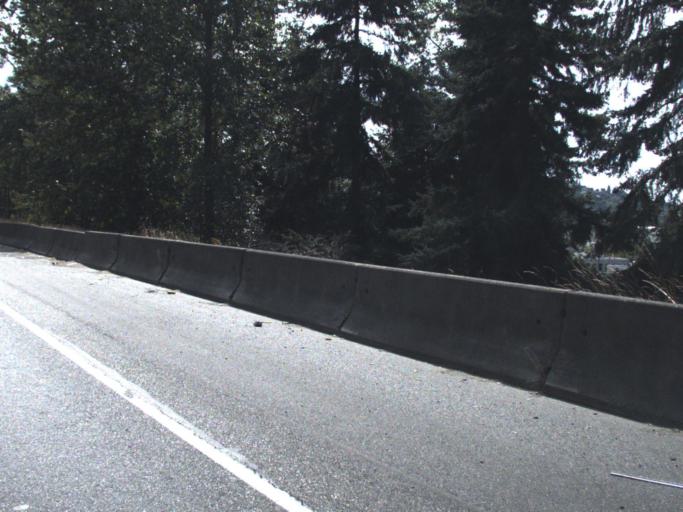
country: US
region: Washington
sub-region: King County
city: Renton
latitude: 47.4947
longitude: -122.1929
